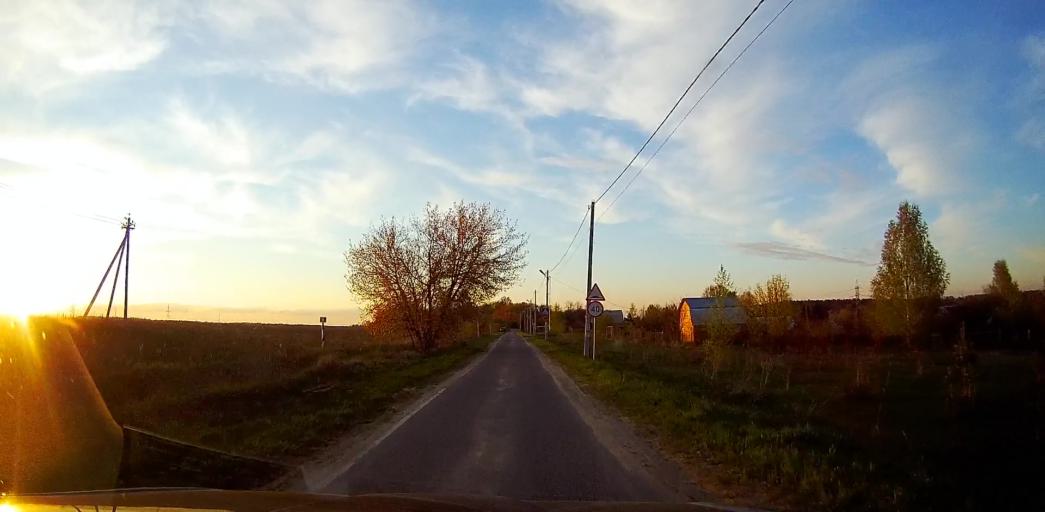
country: RU
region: Moskovskaya
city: Peski
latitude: 55.2289
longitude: 38.7337
